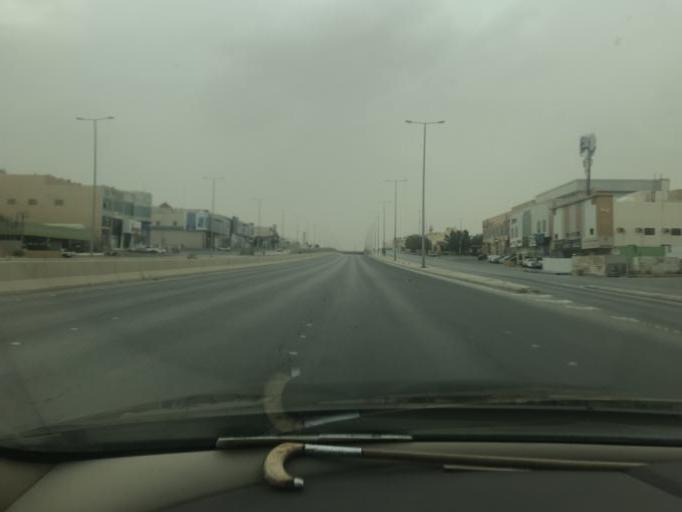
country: SA
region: Ar Riyad
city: Riyadh
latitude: 24.7745
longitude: 46.7099
